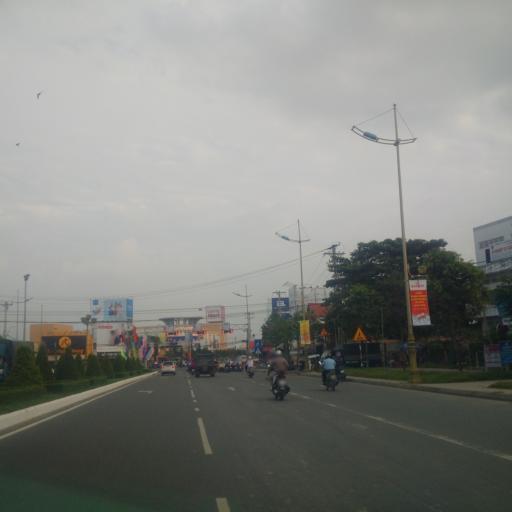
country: VN
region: Can Tho
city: Can Tho
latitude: 10.0450
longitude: 105.7628
